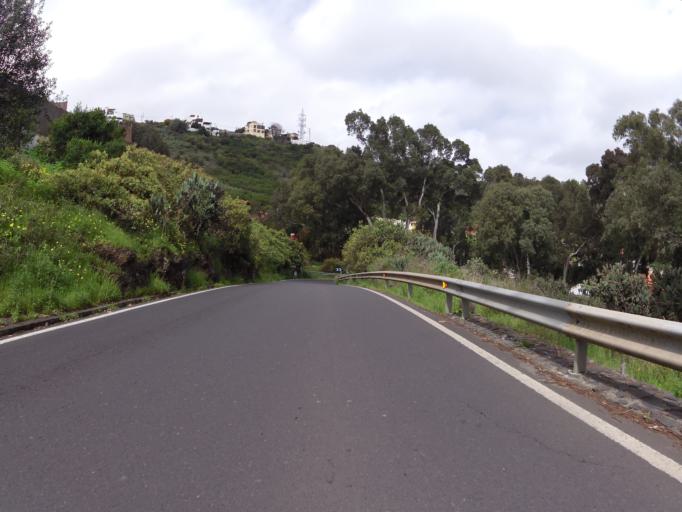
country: ES
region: Canary Islands
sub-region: Provincia de Las Palmas
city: Arucas
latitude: 28.0986
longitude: -15.5332
